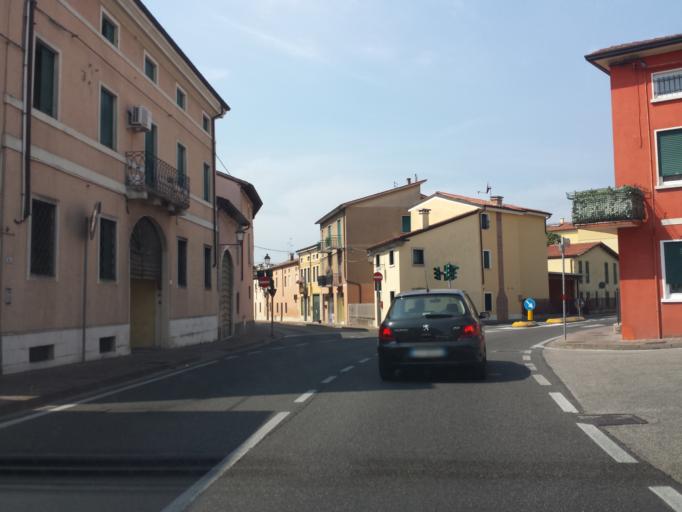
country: IT
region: Veneto
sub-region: Provincia di Vicenza
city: Montecchio Maggiore-Alte Ceccato
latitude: 45.5054
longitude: 11.4187
